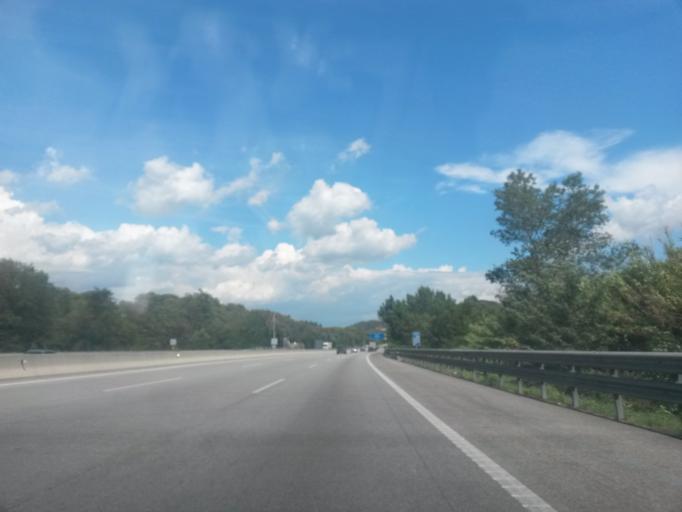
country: ES
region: Catalonia
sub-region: Provincia de Barcelona
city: Sant Celoni
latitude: 41.6683
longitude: 2.4724
